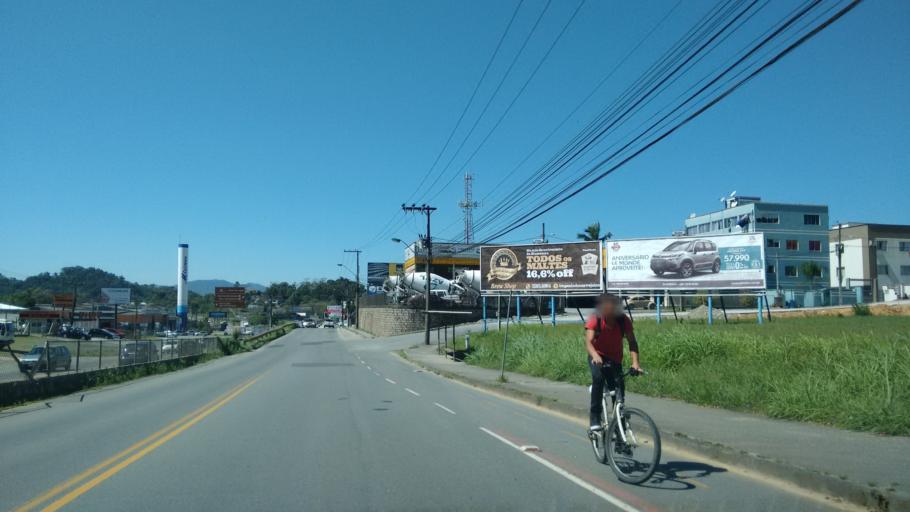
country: BR
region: Santa Catarina
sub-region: Blumenau
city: Blumenau
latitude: -26.8762
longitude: -49.1192
